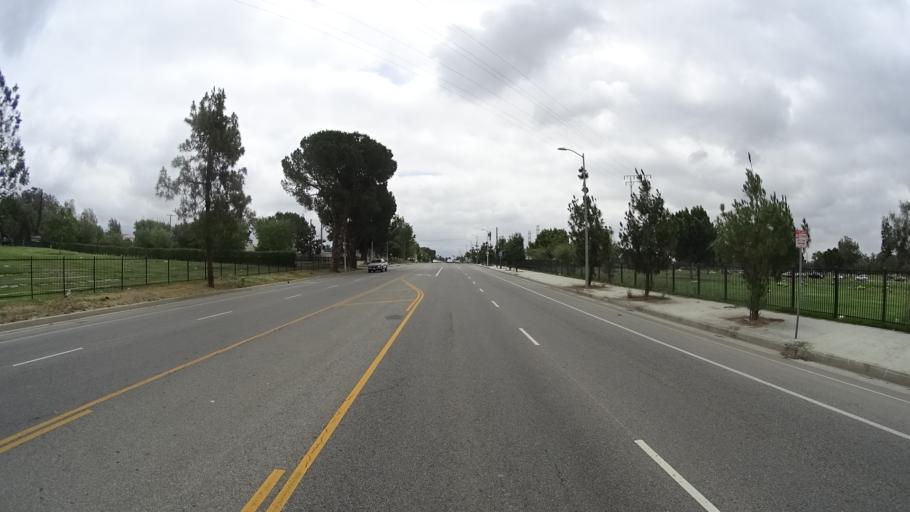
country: US
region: California
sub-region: Los Angeles County
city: San Fernando
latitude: 34.2790
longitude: -118.4662
